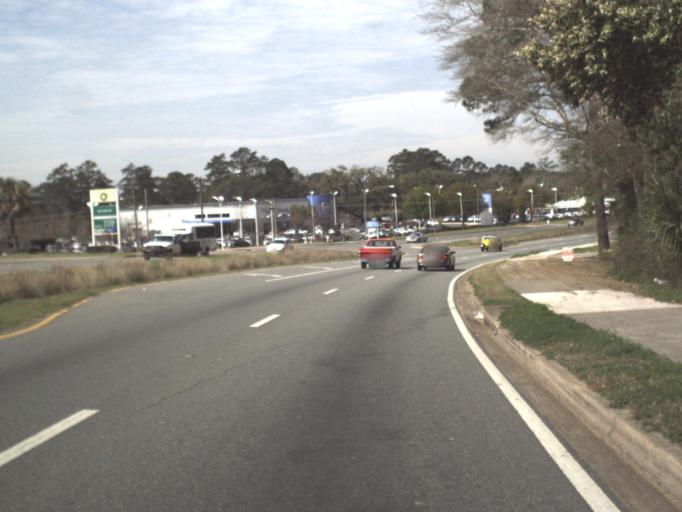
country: US
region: Florida
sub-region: Leon County
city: Tallahassee
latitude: 30.4460
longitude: -84.3223
